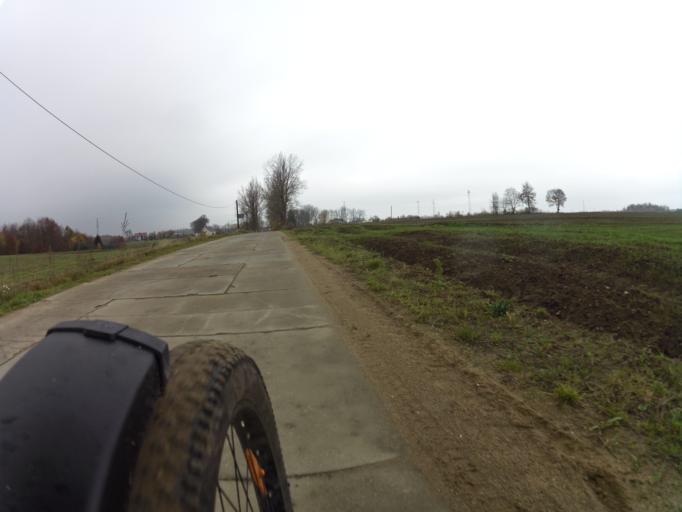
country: PL
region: Pomeranian Voivodeship
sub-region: Powiat pucki
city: Krokowa
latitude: 54.7198
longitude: 18.1382
